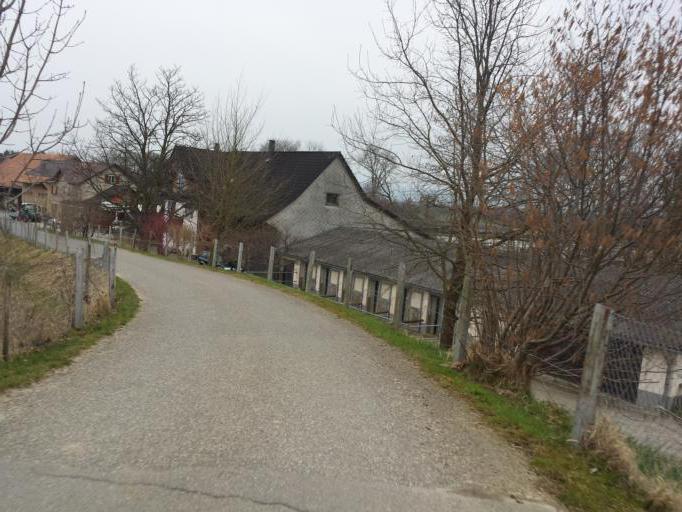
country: CH
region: Thurgau
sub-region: Arbon District
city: Salmsach
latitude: 47.5512
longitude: 9.3467
